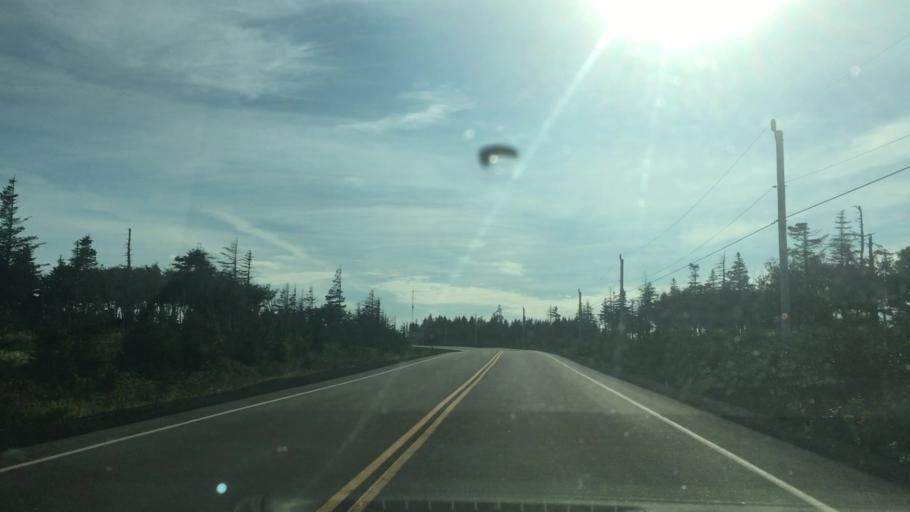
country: CA
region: Nova Scotia
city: Sydney Mines
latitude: 46.8234
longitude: -60.6608
